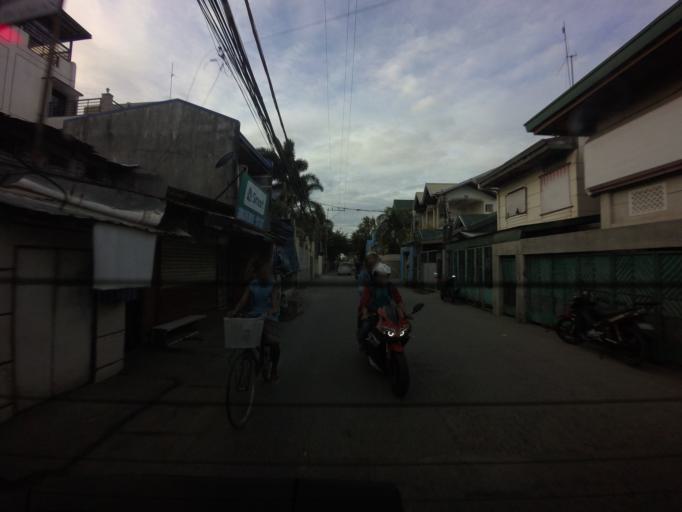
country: PH
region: Central Luzon
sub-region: Province of Bulacan
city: Obando
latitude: 14.7227
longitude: 120.9282
